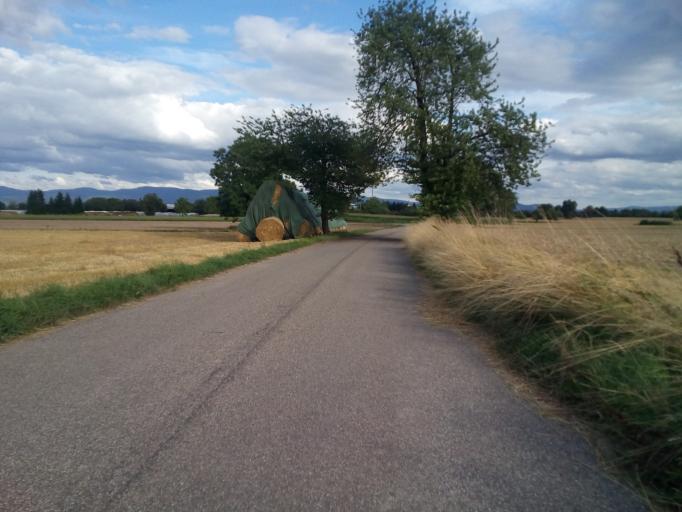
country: DE
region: Baden-Wuerttemberg
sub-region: Karlsruhe Region
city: Lichtenau
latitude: 48.7181
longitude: 7.9875
